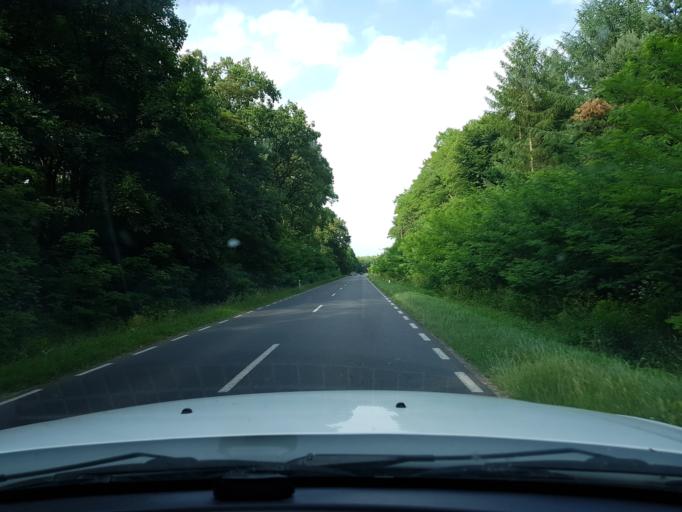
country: PL
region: West Pomeranian Voivodeship
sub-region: Powiat gryfinski
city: Chojna
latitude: 52.9284
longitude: 14.3741
